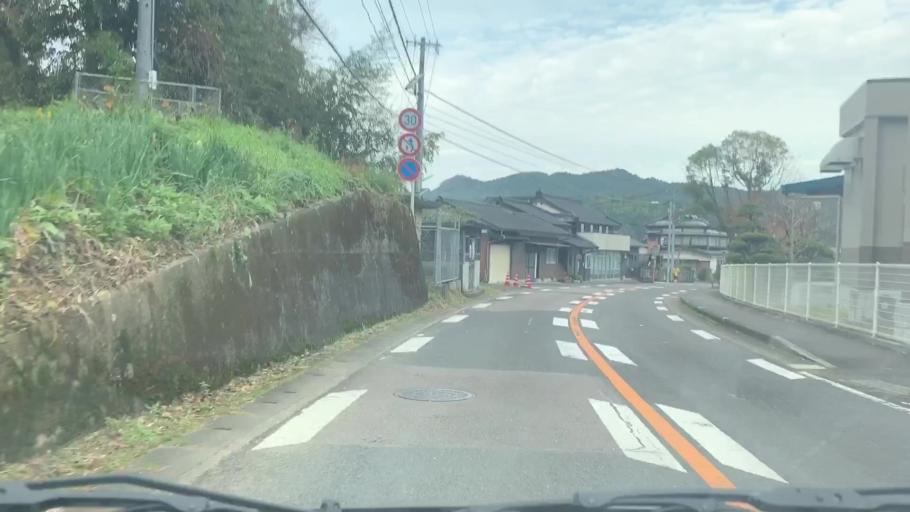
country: JP
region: Saga Prefecture
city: Takeocho-takeo
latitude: 33.1931
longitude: 129.9640
